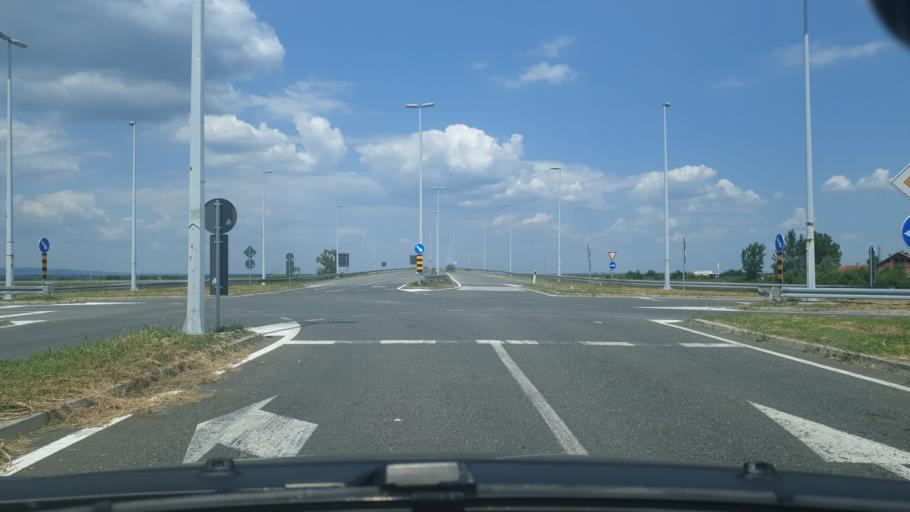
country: RS
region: Autonomna Pokrajina Vojvodina
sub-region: Sremski Okrug
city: Pecinci
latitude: 44.9173
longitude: 19.9574
